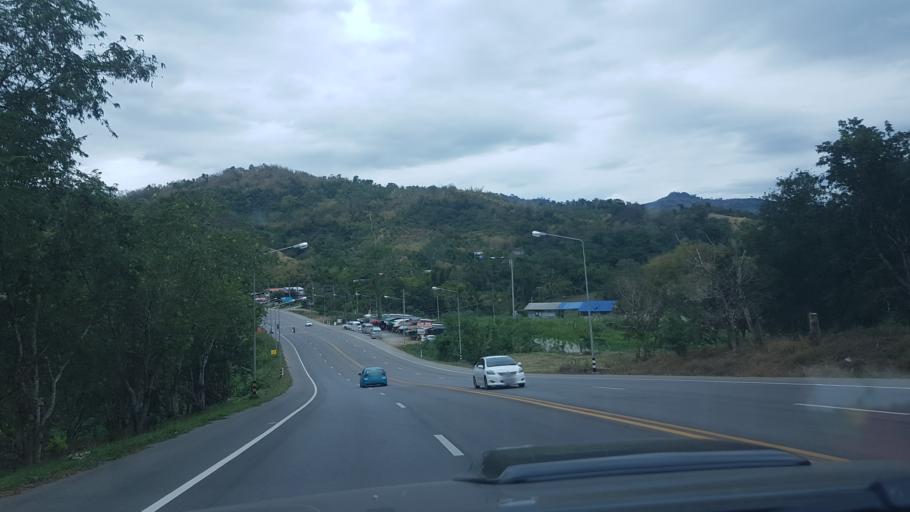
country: TH
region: Phetchabun
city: Khao Kho
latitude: 16.5422
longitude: 101.0552
